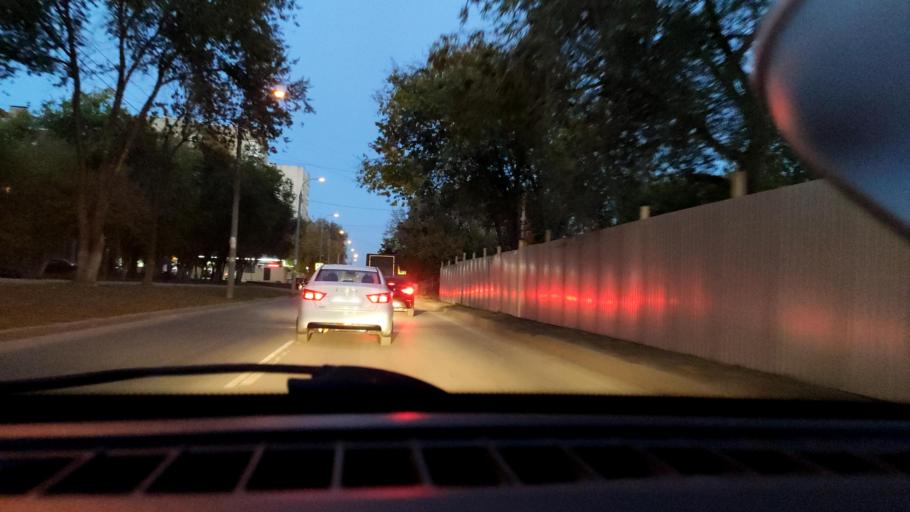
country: RU
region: Samara
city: Samara
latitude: 53.1872
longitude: 50.1861
